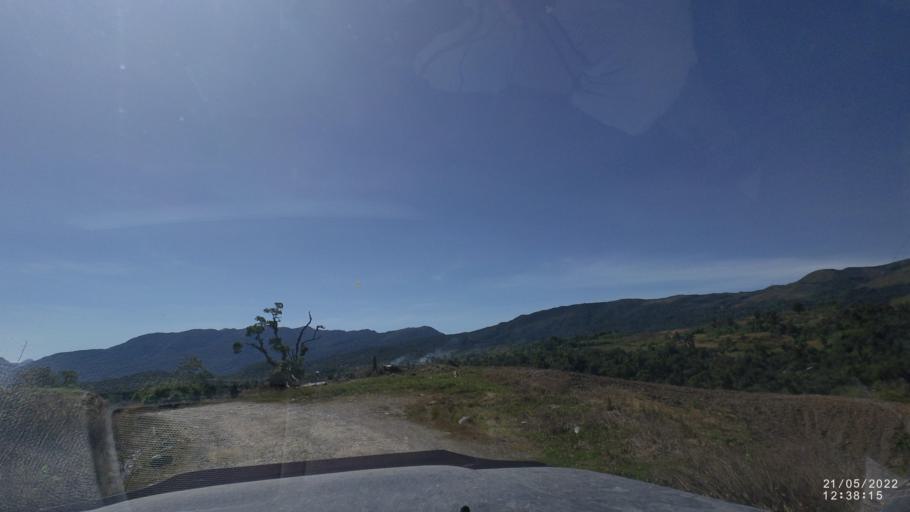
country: BO
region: Cochabamba
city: Colomi
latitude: -17.2010
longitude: -65.9201
